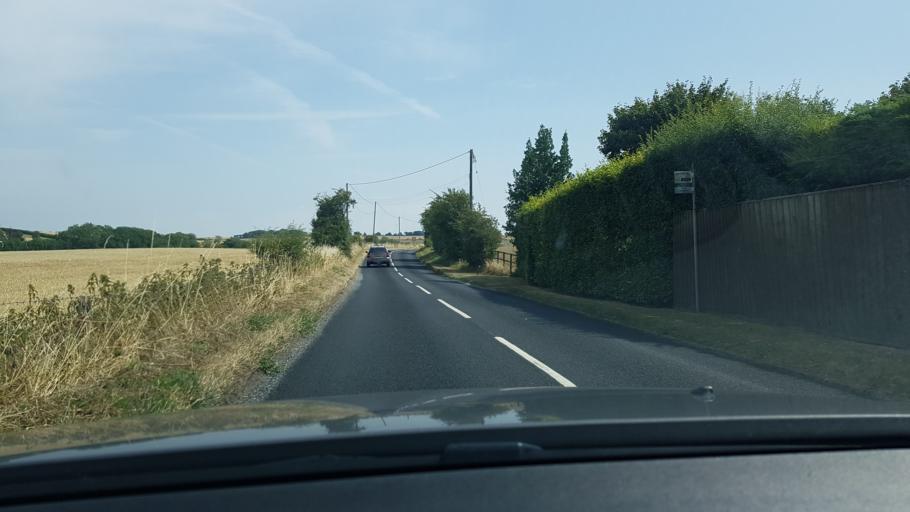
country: GB
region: England
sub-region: West Berkshire
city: Lambourn
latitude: 51.4891
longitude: -1.4871
